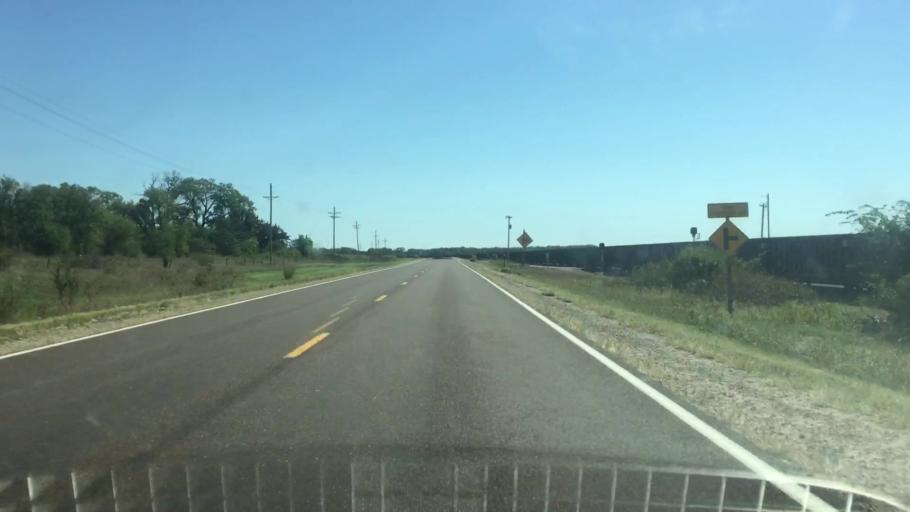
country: US
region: Nebraska
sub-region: Jefferson County
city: Fairbury
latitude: 40.0897
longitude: -97.1223
